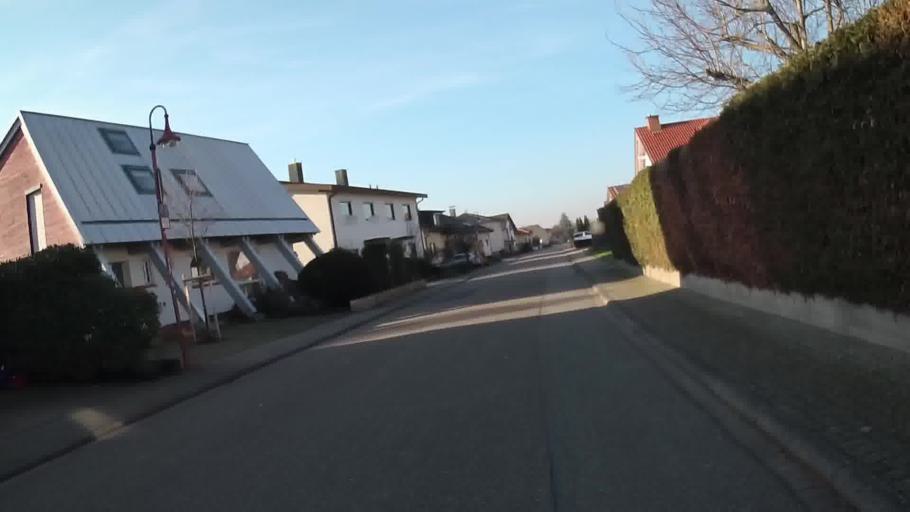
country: DE
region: Baden-Wuerttemberg
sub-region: Karlsruhe Region
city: Malsch
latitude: 49.2415
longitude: 8.6788
